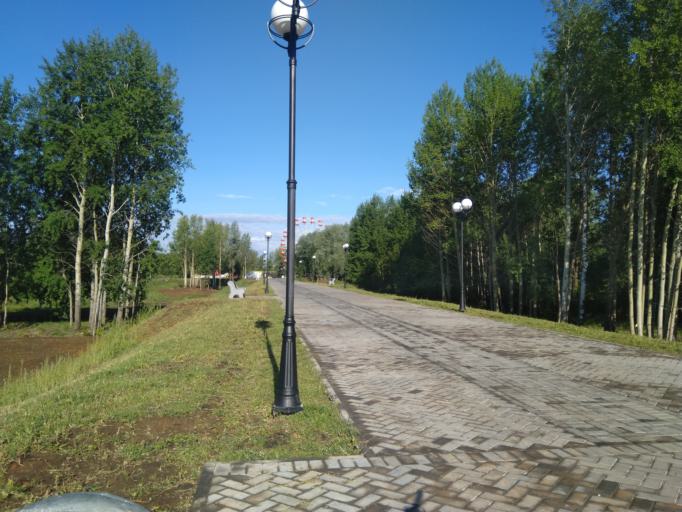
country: RU
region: Chuvashia
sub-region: Cheboksarskiy Rayon
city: Cheboksary
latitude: 56.1479
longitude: 47.2089
